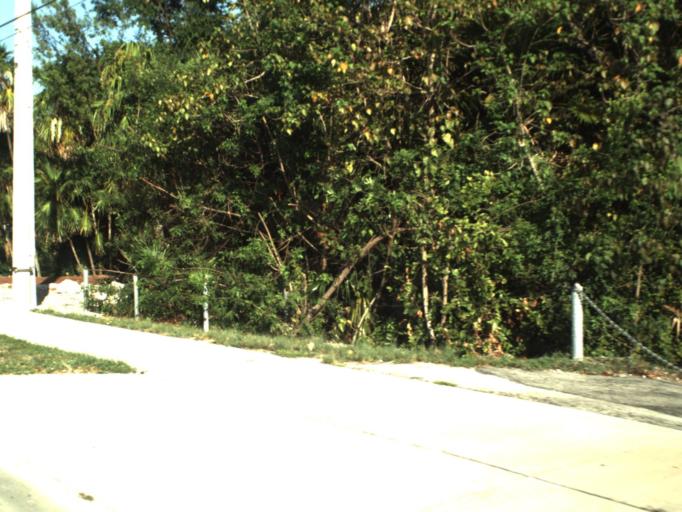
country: US
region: Florida
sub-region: Monroe County
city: Marathon
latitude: 24.7252
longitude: -81.0488
